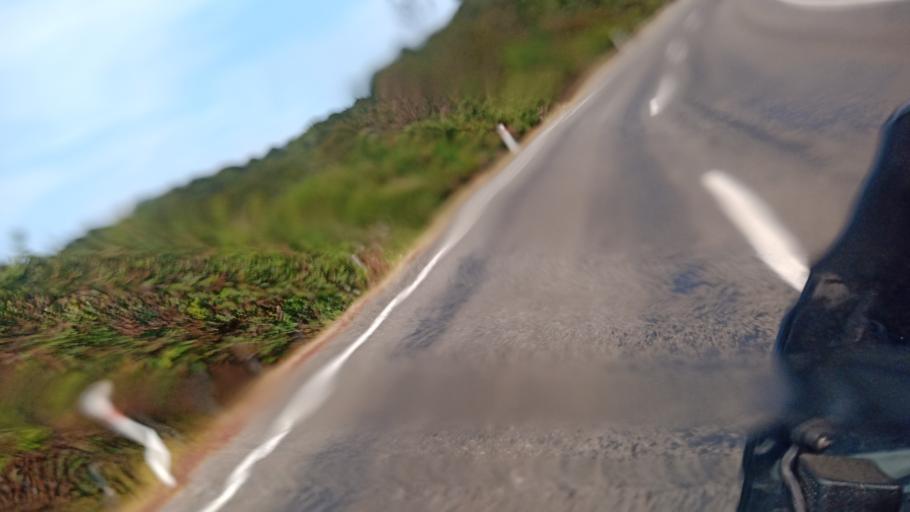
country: NZ
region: Bay of Plenty
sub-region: Opotiki District
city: Opotiki
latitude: -37.5913
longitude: 178.2291
